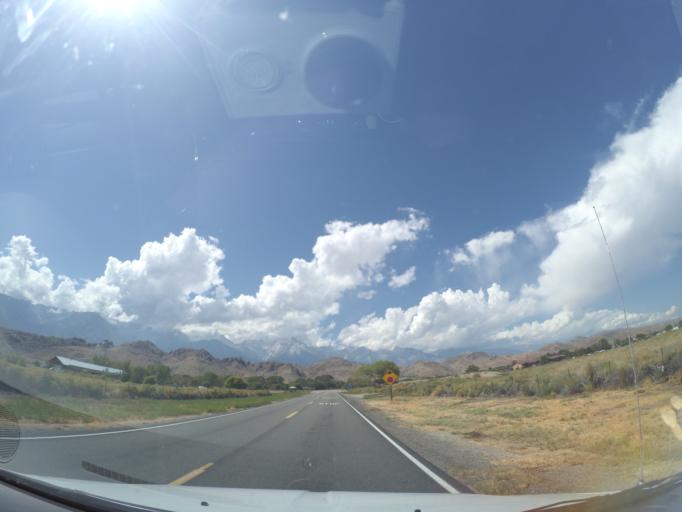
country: US
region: California
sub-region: Inyo County
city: Lone Pine
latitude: 36.5793
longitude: -118.0538
